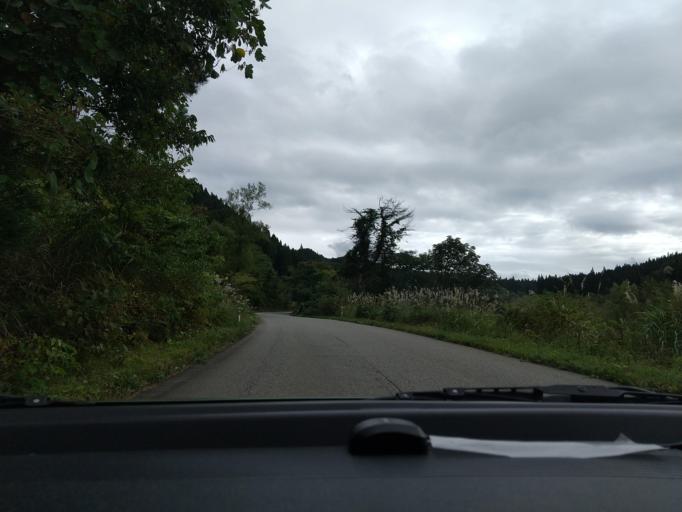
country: JP
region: Akita
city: Kakunodatemachi
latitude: 39.5731
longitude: 140.6320
